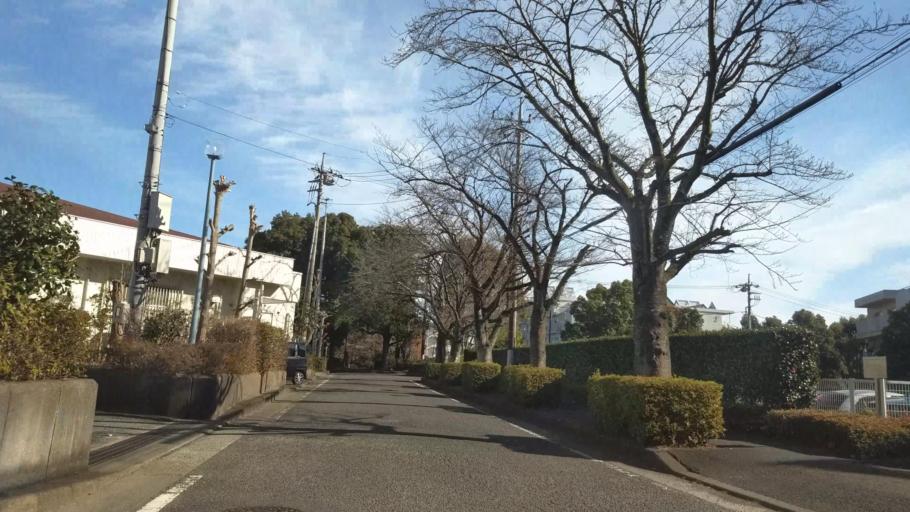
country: JP
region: Kanagawa
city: Hadano
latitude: 35.3541
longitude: 139.2272
